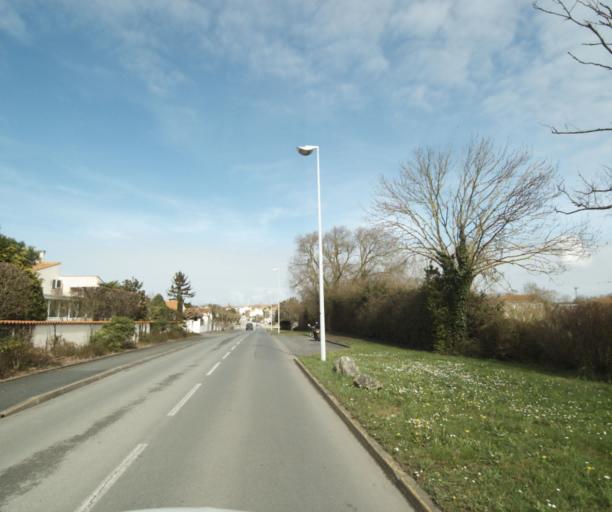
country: FR
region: Poitou-Charentes
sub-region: Departement de la Charente-Maritime
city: Lagord
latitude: 46.1800
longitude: -1.1557
